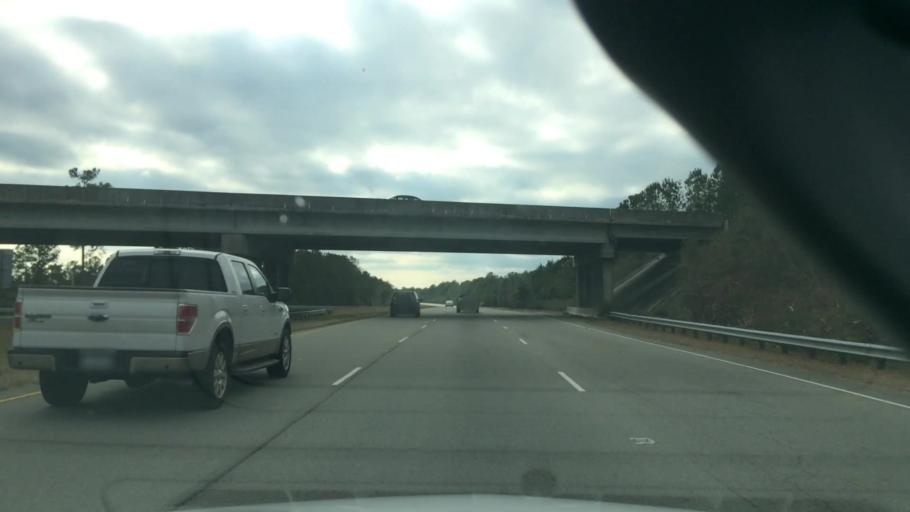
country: US
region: North Carolina
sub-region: Brunswick County
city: Shallotte
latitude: 33.9768
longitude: -78.4045
